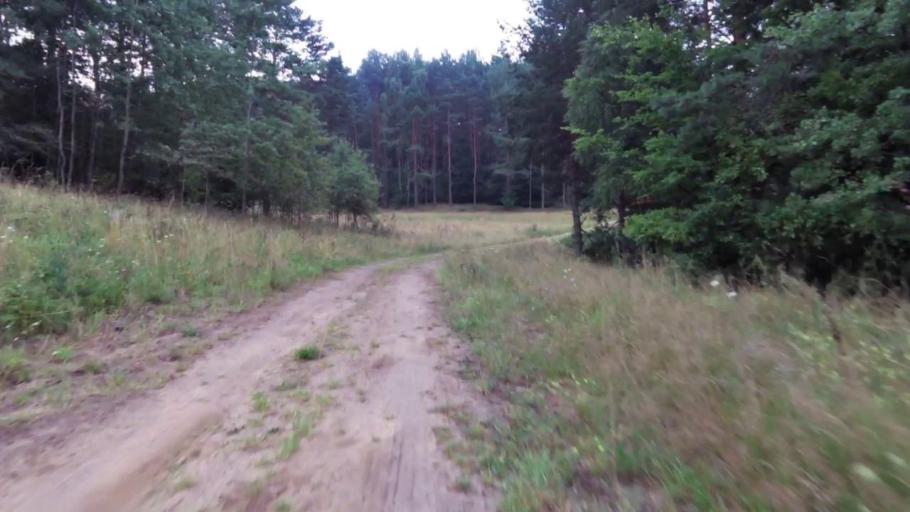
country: PL
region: West Pomeranian Voivodeship
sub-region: Powiat szczecinecki
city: Lubowo
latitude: 53.6015
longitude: 16.3851
